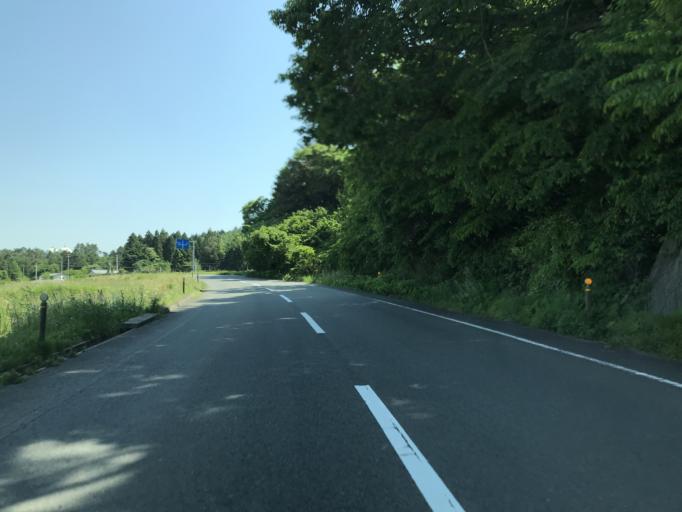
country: JP
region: Miyagi
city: Marumori
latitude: 37.8003
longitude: 140.8814
